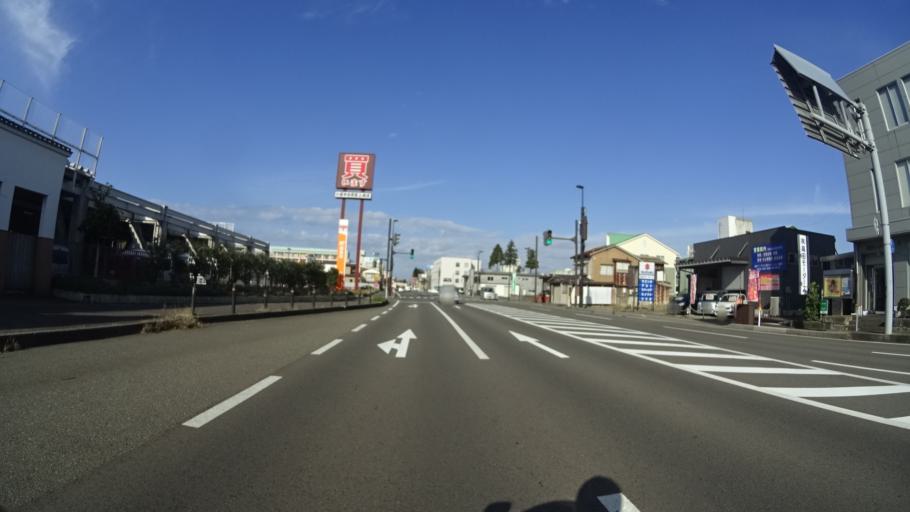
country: JP
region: Niigata
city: Joetsu
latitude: 37.1092
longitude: 138.2503
